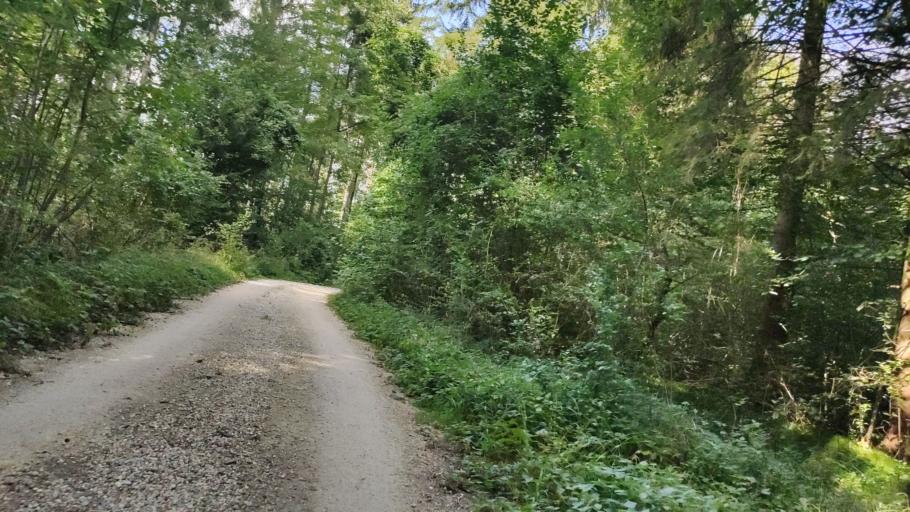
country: DE
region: Bavaria
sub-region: Swabia
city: Klosterlechfeld
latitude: 48.1342
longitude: 10.8615
